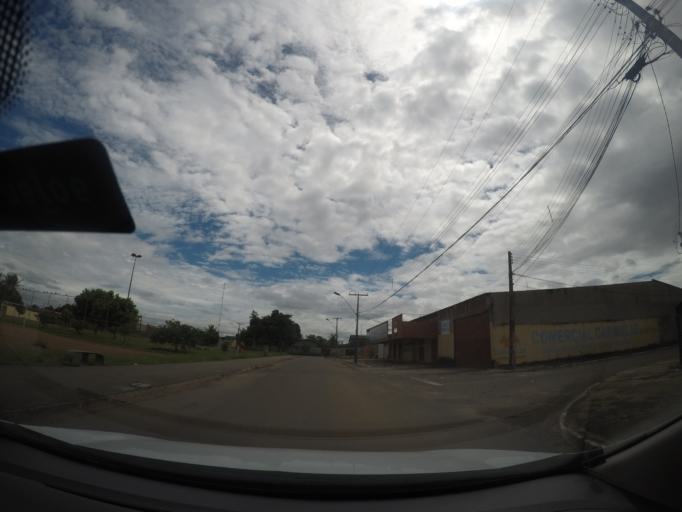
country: BR
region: Goias
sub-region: Goiania
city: Goiania
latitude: -16.7576
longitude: -49.3507
